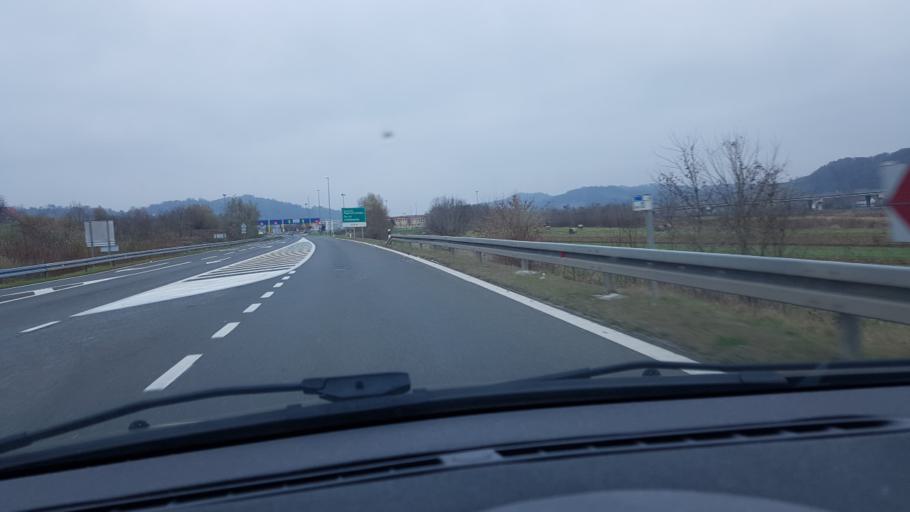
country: HR
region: Krapinsko-Zagorska
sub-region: Grad Krapina
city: Krapina
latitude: 46.1348
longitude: 15.8811
